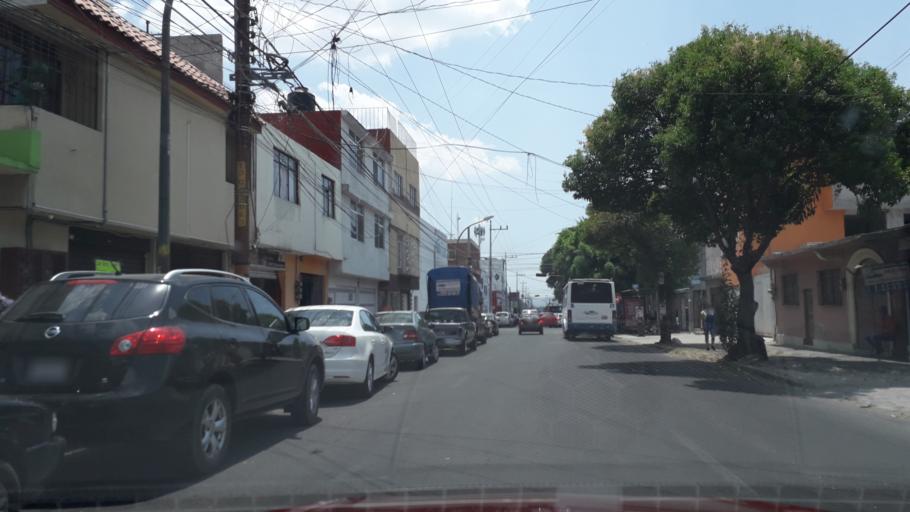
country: MX
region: Puebla
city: Puebla
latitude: 19.0425
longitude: -98.2169
